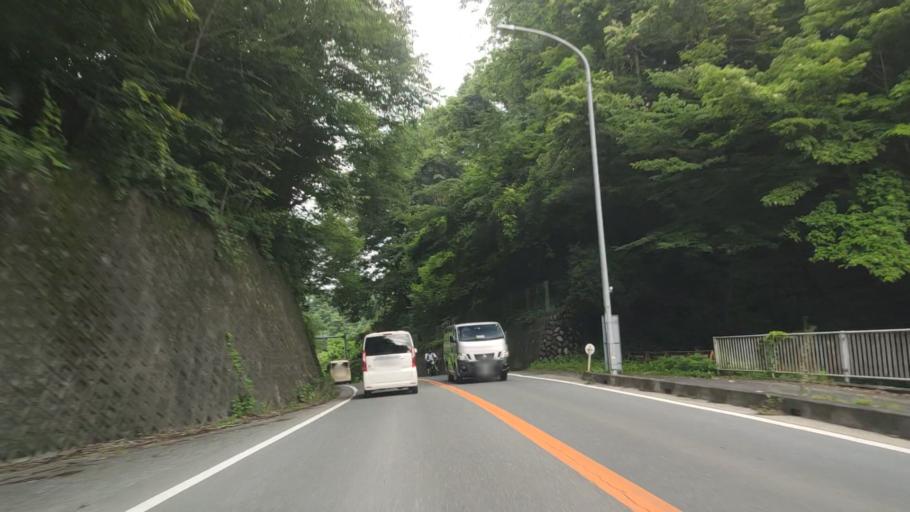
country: JP
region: Saitama
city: Chichibu
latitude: 36.0090
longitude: 139.0473
